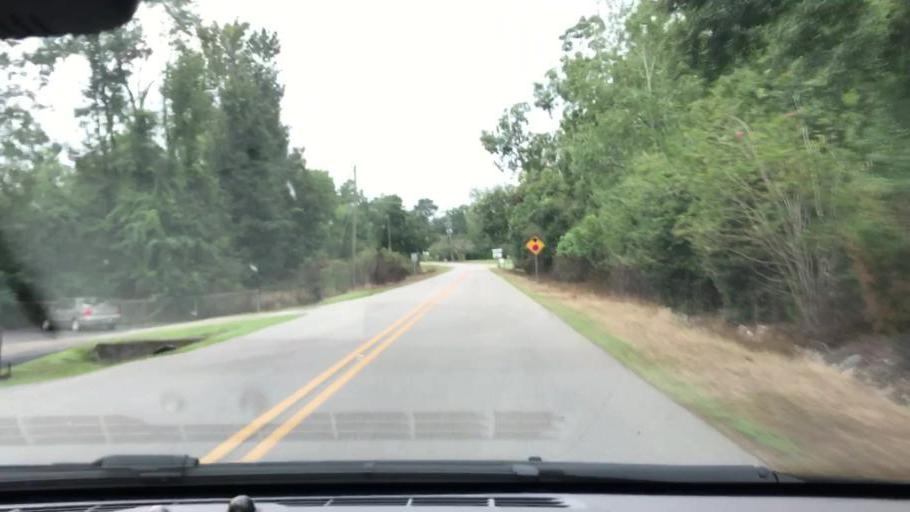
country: US
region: Alabama
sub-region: Houston County
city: Ashford
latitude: 31.1897
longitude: -85.2335
